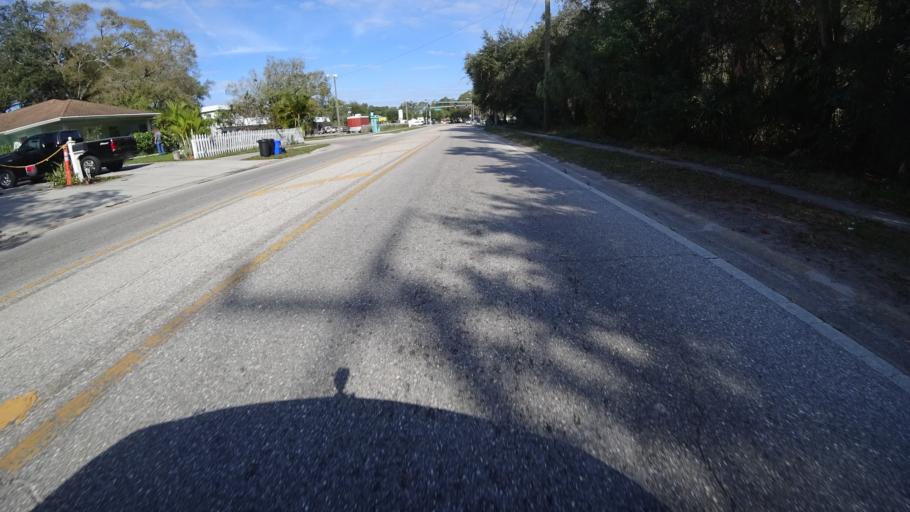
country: US
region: Florida
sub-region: Manatee County
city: Whitfield
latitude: 27.4391
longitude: -82.5590
